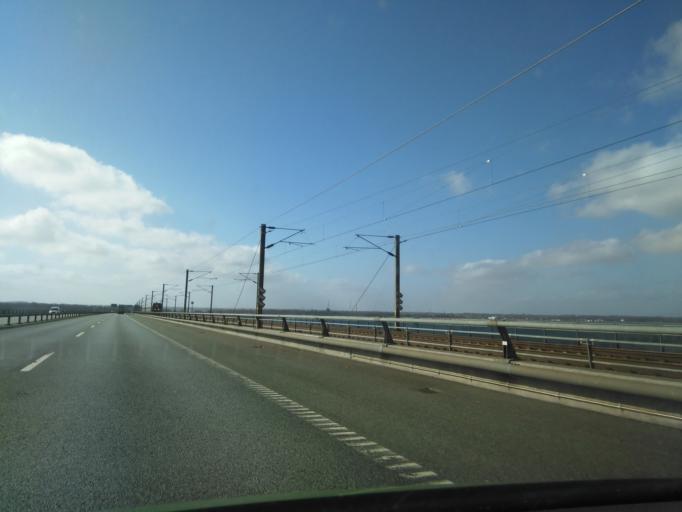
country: DK
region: South Denmark
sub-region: Nyborg Kommune
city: Nyborg
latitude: 55.3012
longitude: 10.8613
